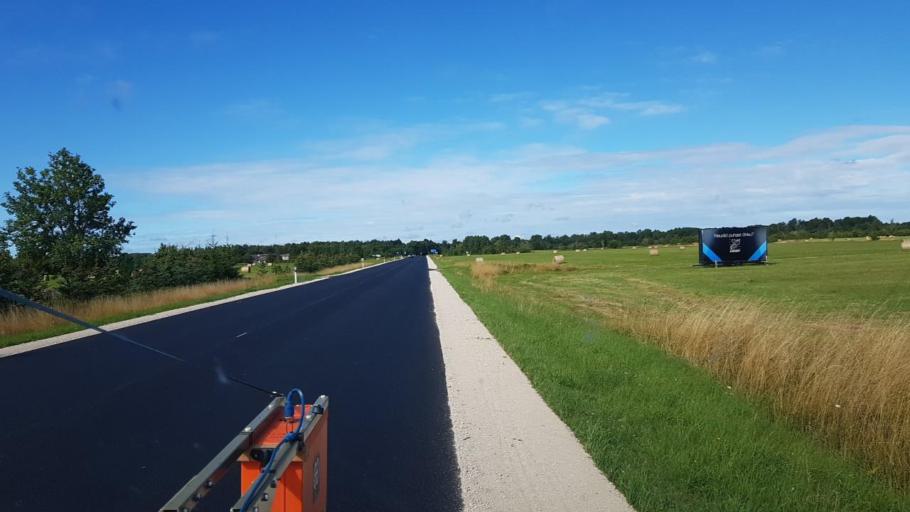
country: EE
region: Saare
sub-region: Orissaare vald
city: Orissaare
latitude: 58.6075
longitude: 23.2660
